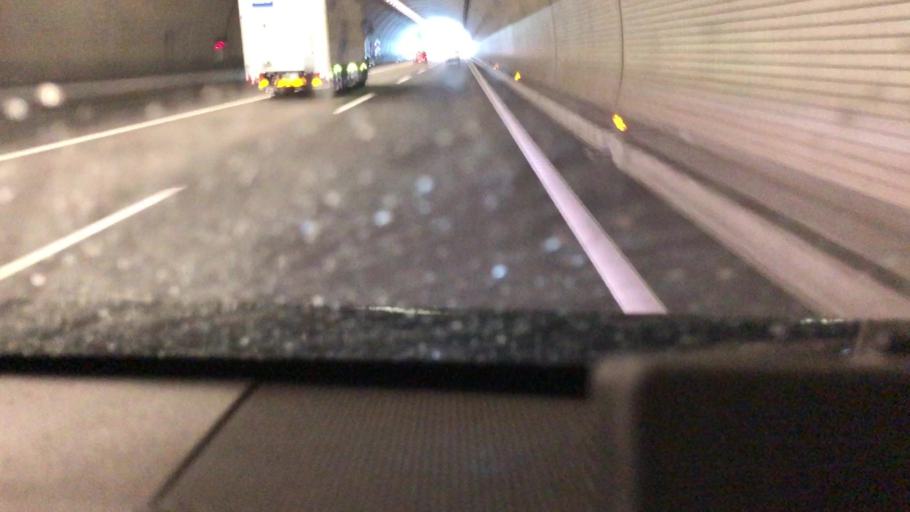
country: JP
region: Shizuoka
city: Numazu
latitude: 35.1560
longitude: 138.7906
